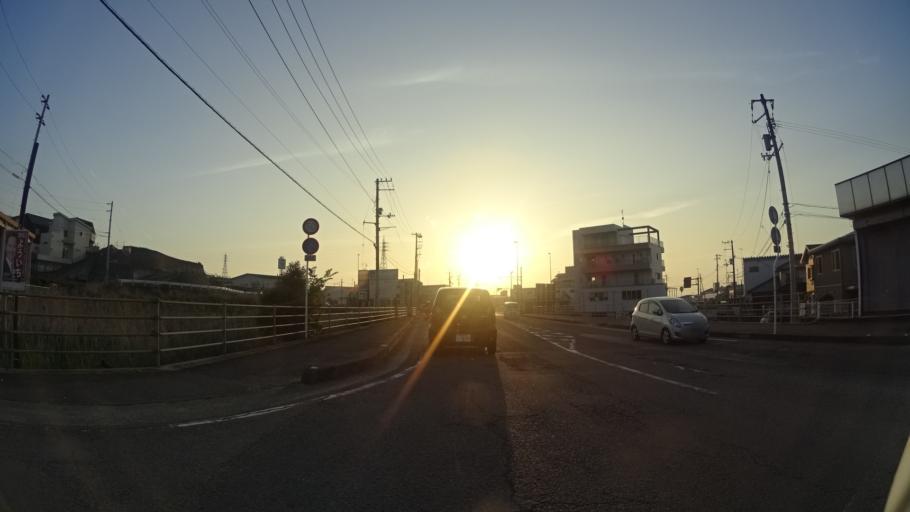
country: JP
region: Ehime
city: Kawanoecho
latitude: 33.9909
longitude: 133.5823
